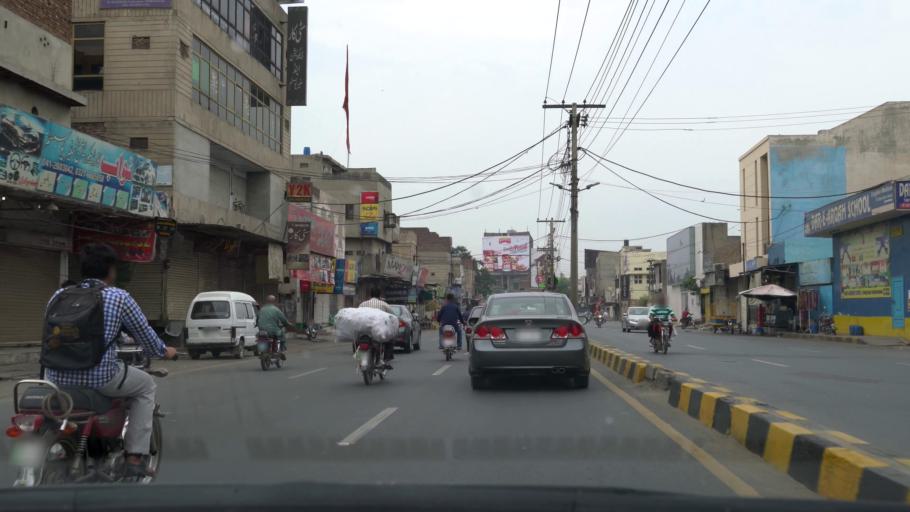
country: PK
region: Punjab
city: Faisalabad
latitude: 31.4240
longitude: 73.0705
